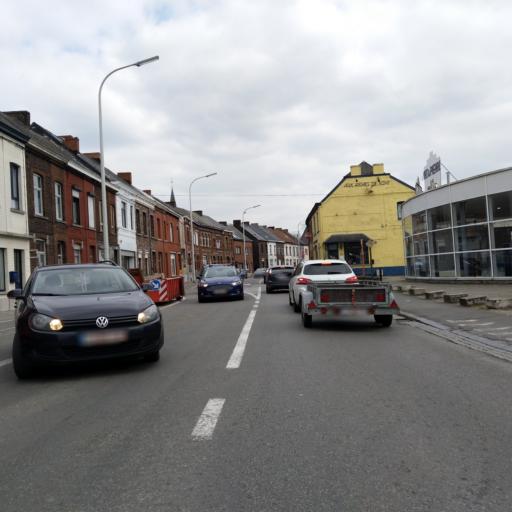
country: BE
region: Wallonia
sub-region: Province du Hainaut
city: Mons
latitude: 50.4774
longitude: 3.9532
